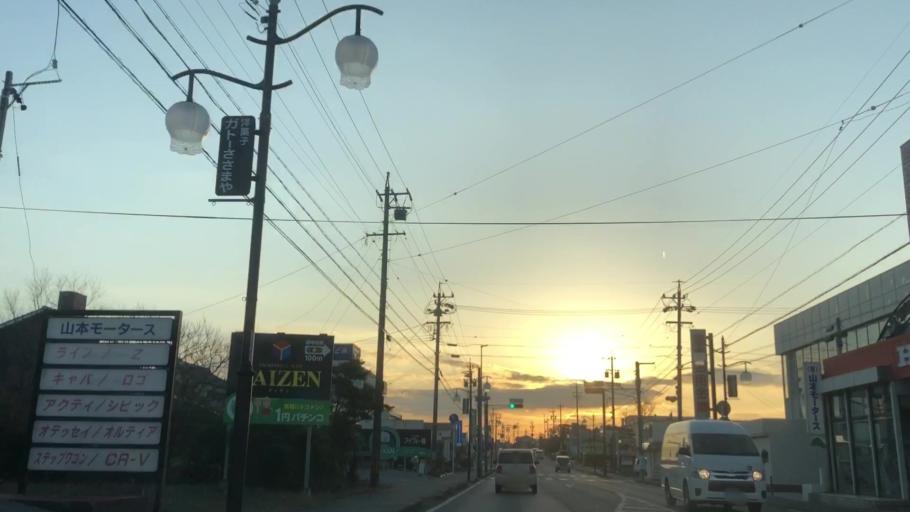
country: JP
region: Aichi
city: Tahara
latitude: 34.6249
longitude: 137.0995
